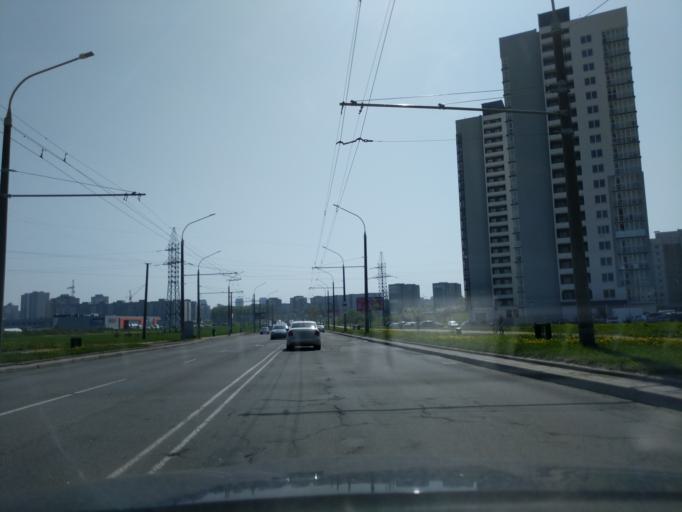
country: BY
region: Minsk
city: Novoye Medvezhino
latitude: 53.8776
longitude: 27.4600
